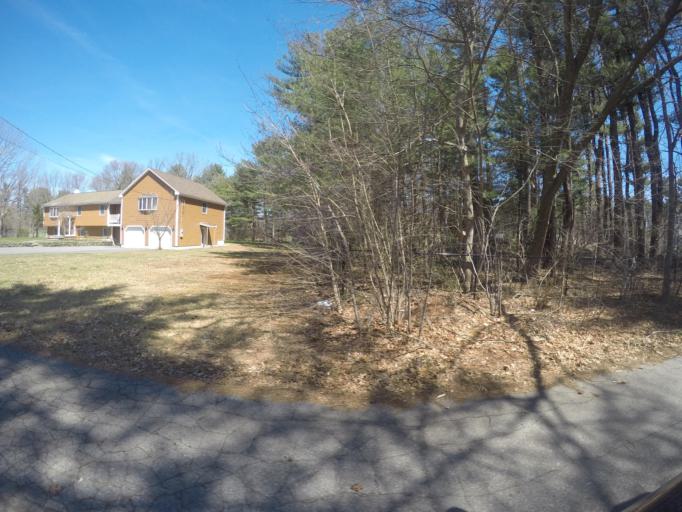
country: US
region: Massachusetts
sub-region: Bristol County
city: Easton
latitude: 42.0388
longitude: -71.0840
